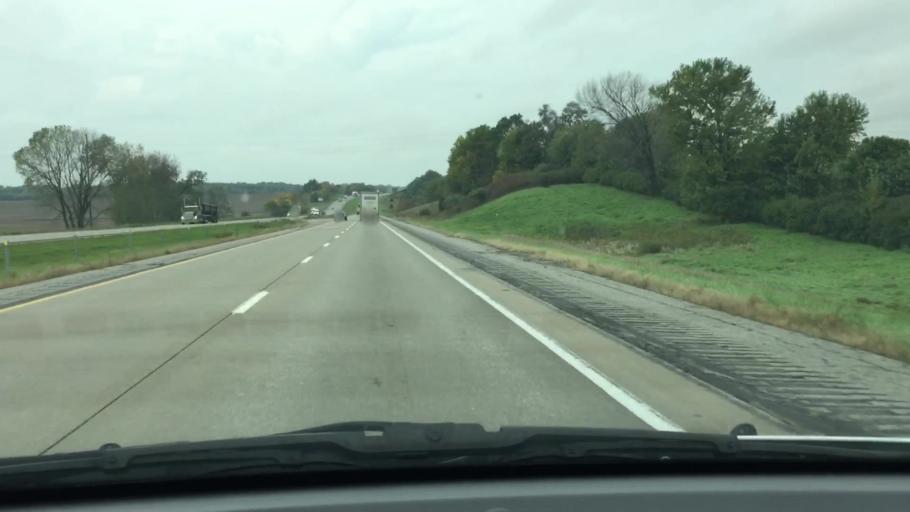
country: US
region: Iowa
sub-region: Cedar County
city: West Branch
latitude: 41.6682
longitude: -91.3833
